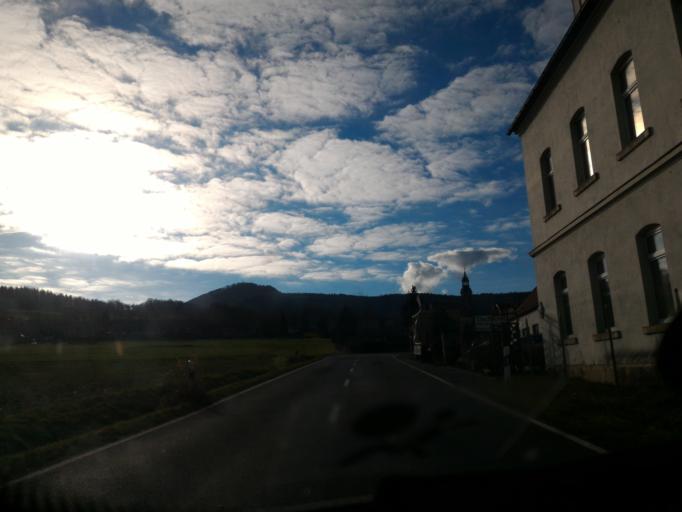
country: DE
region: Saxony
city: Grossschonau
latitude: 50.8721
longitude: 14.6533
